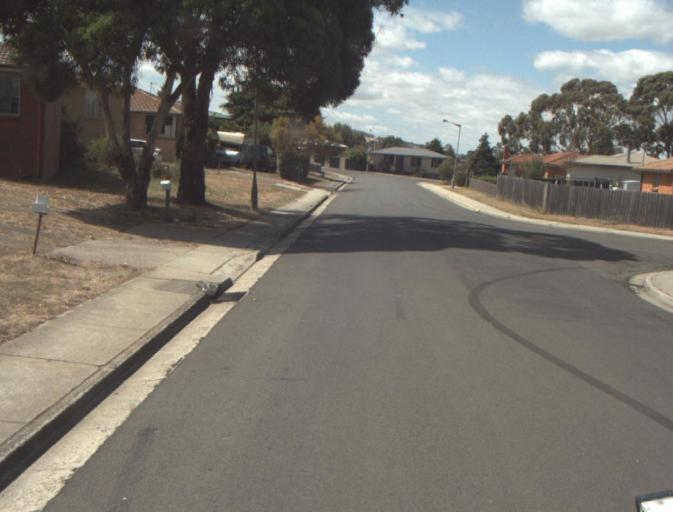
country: AU
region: Tasmania
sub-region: Launceston
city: Newstead
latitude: -41.4130
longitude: 147.1739
